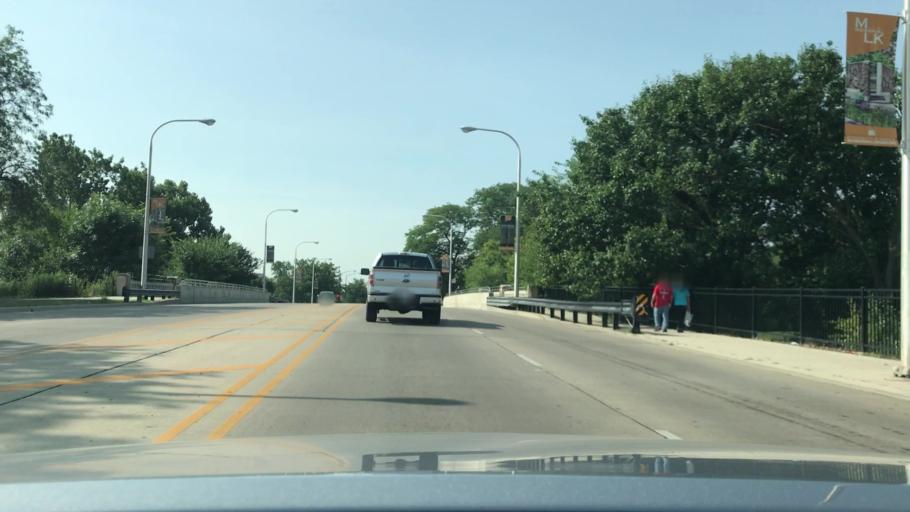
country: US
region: Illinois
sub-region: Cook County
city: Hometown
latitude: 41.7665
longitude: -87.7029
